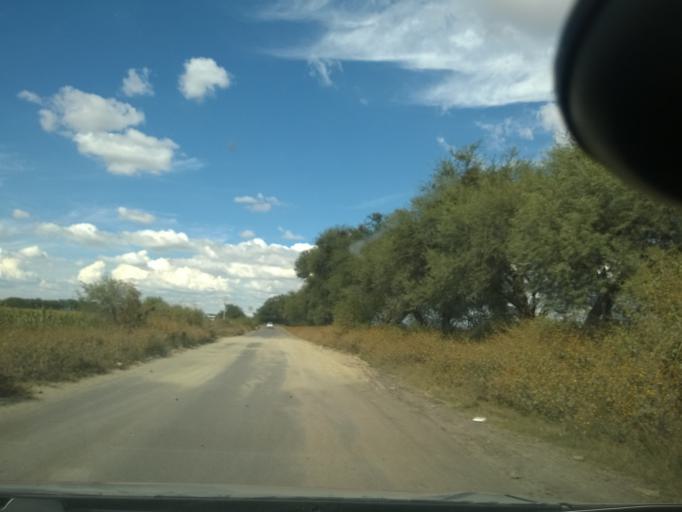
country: MX
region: Guanajuato
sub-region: Leon
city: Plan Guanajuato (La Sandia)
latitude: 20.9035
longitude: -101.6308
